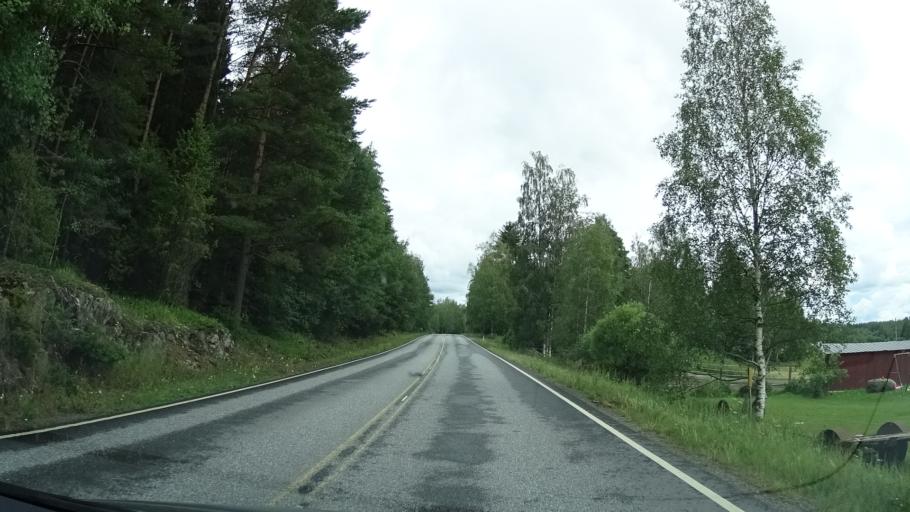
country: FI
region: Haeme
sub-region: Forssa
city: Humppila
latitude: 61.0933
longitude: 23.3732
